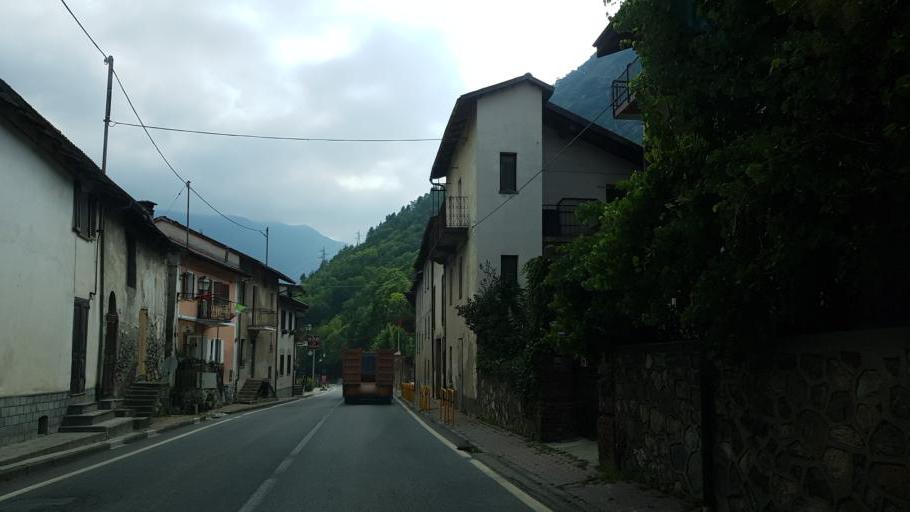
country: IT
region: Piedmont
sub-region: Provincia di Cuneo
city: Moiola
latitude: 44.3188
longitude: 7.3886
